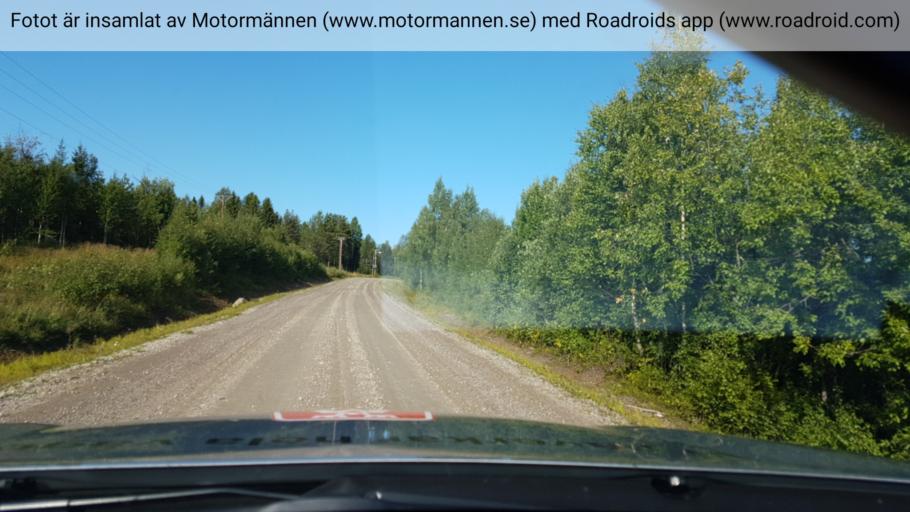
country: SE
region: Norrbotten
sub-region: Kalix Kommun
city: Kalix
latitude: 66.1357
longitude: 23.2355
